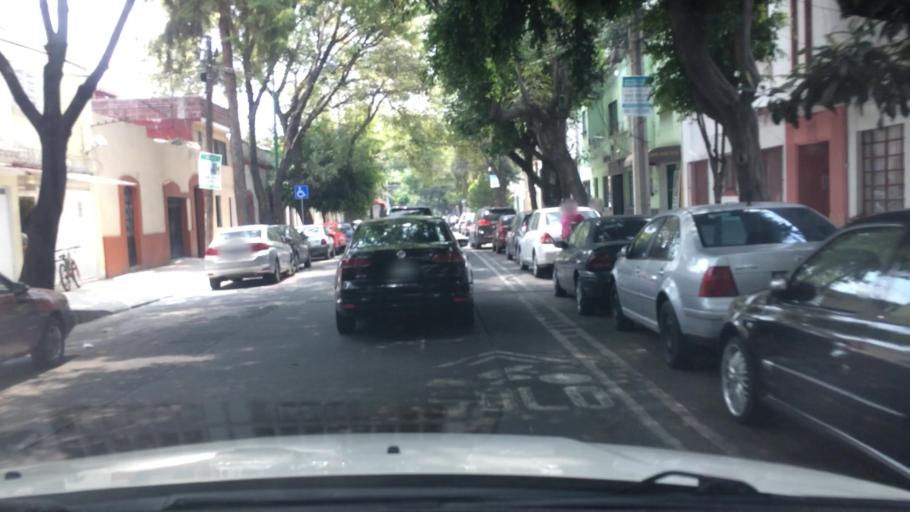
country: MX
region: Mexico City
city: Benito Juarez
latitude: 19.4009
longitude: -99.1768
